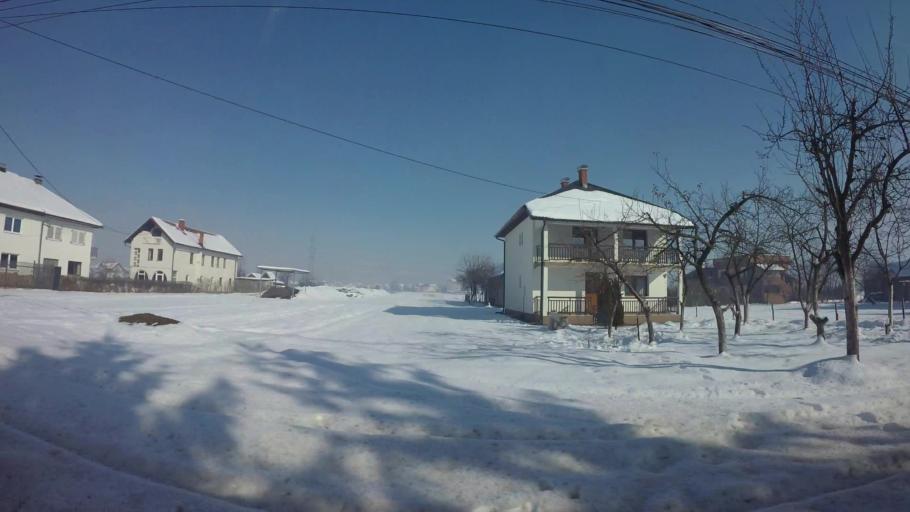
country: BA
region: Federation of Bosnia and Herzegovina
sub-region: Kanton Sarajevo
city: Sarajevo
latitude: 43.8052
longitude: 18.3025
